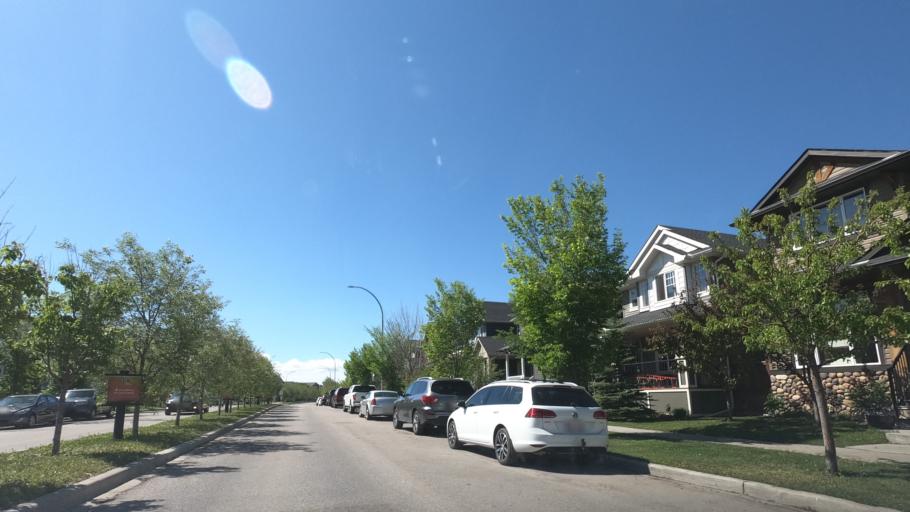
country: CA
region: Alberta
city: Airdrie
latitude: 51.2699
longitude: -113.9722
